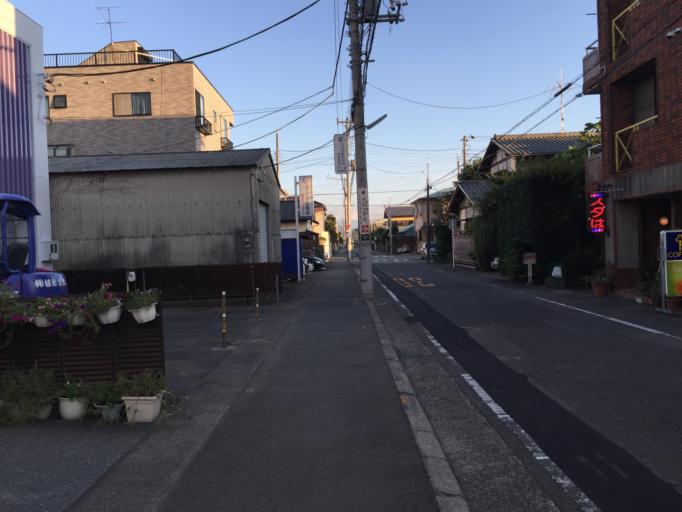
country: JP
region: Shizuoka
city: Numazu
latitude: 35.0939
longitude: 138.8633
